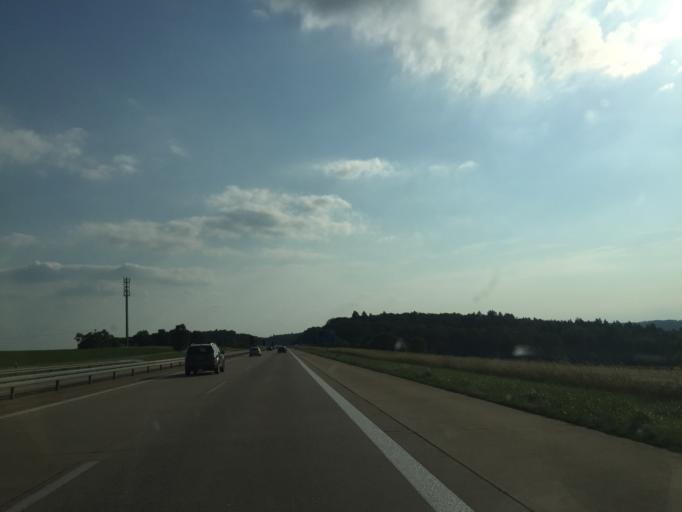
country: DE
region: Baden-Wuerttemberg
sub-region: Regierungsbezirk Stuttgart
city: Widdern
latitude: 49.3704
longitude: 9.4424
